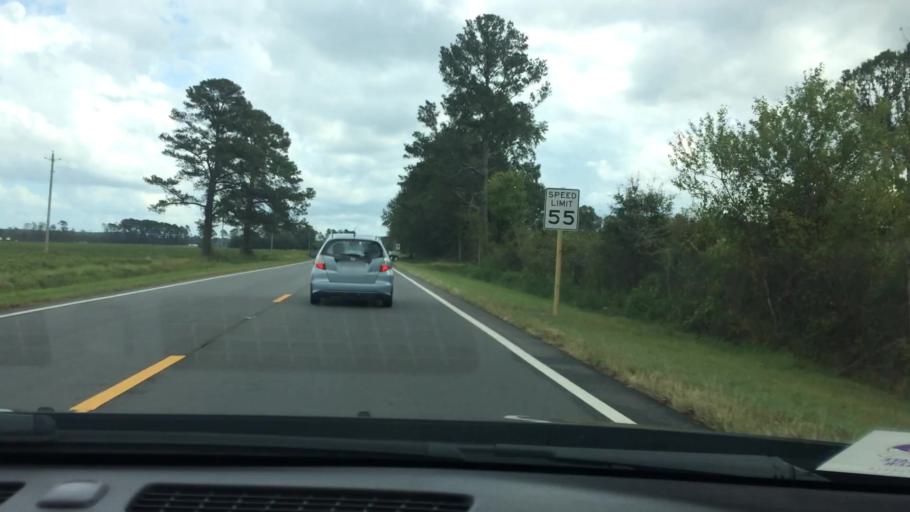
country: US
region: North Carolina
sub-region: Pitt County
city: Farmville
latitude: 35.6016
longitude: -77.6432
